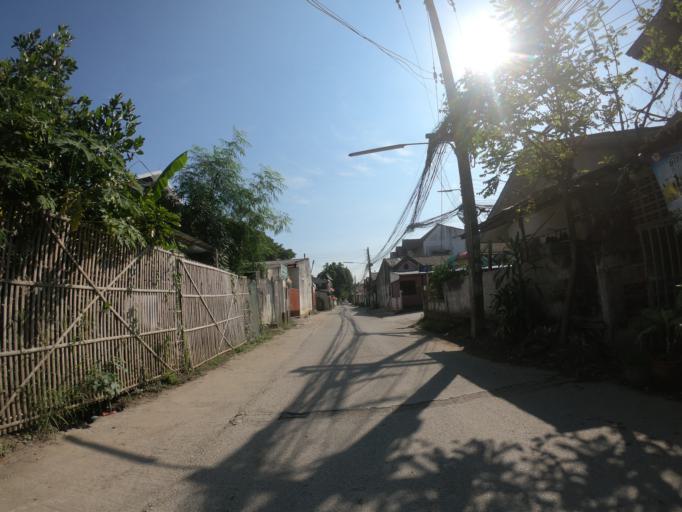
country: TH
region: Chiang Mai
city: Chiang Mai
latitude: 18.7526
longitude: 99.0031
